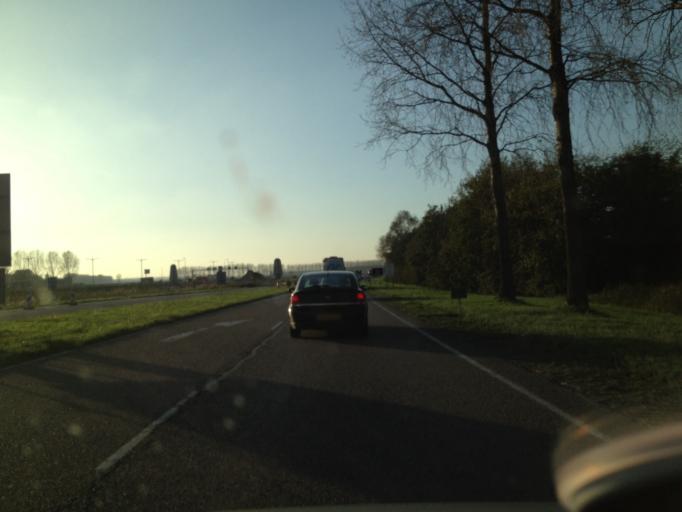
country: NL
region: Zeeland
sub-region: Gemeente Terneuzen
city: Sluiskil
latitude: 51.2928
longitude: 3.8257
